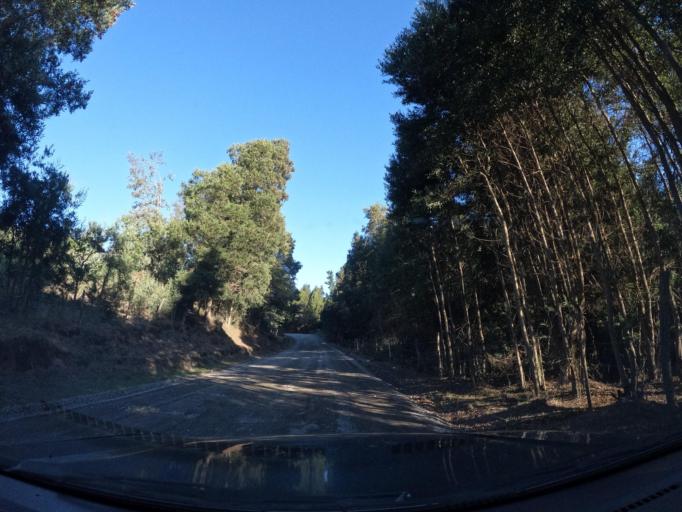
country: CL
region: Biobio
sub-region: Provincia de Concepcion
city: Chiguayante
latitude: -37.0186
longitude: -72.8919
